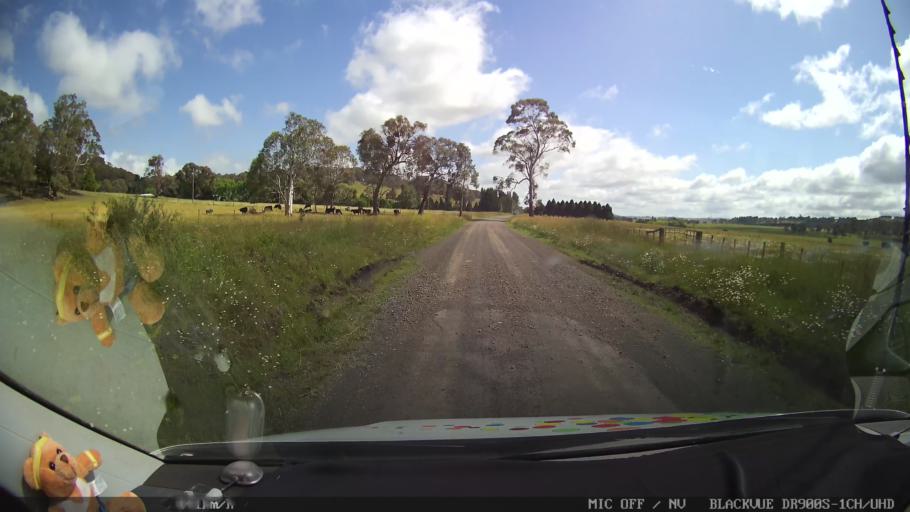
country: AU
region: New South Wales
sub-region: Glen Innes Severn
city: Glen Innes
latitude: -29.9626
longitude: 151.6999
